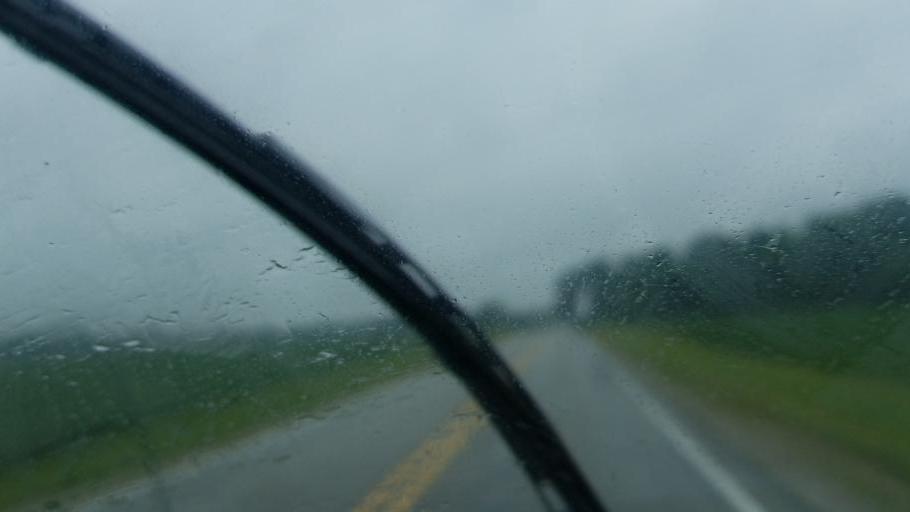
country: US
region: Indiana
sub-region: Huntington County
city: Warren
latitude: 40.6566
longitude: -85.3999
